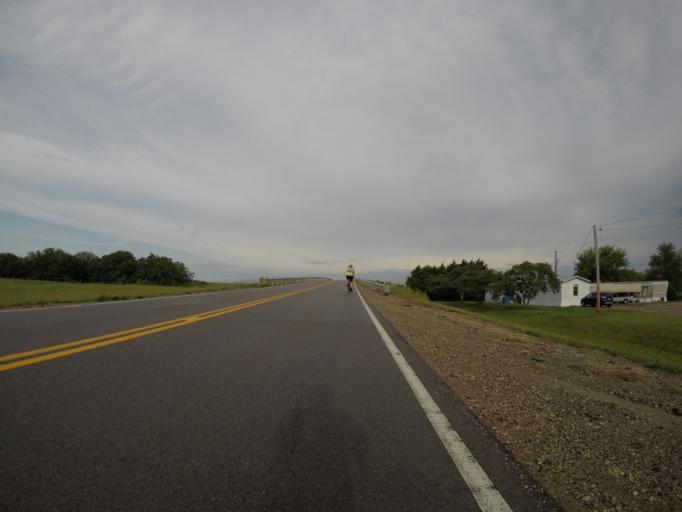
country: US
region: Kansas
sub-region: Shawnee County
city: Auburn
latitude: 38.9568
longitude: -95.7328
